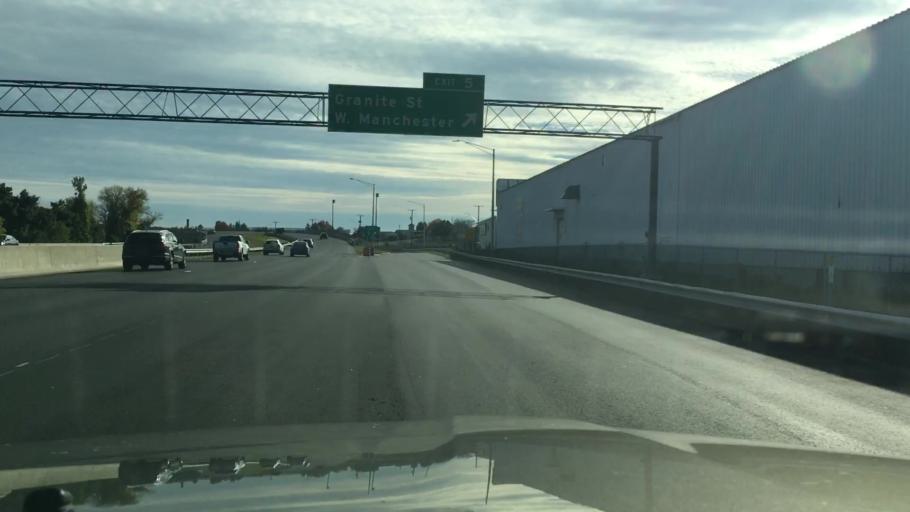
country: US
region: New Hampshire
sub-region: Hillsborough County
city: Manchester
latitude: 42.9893
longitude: -71.4716
